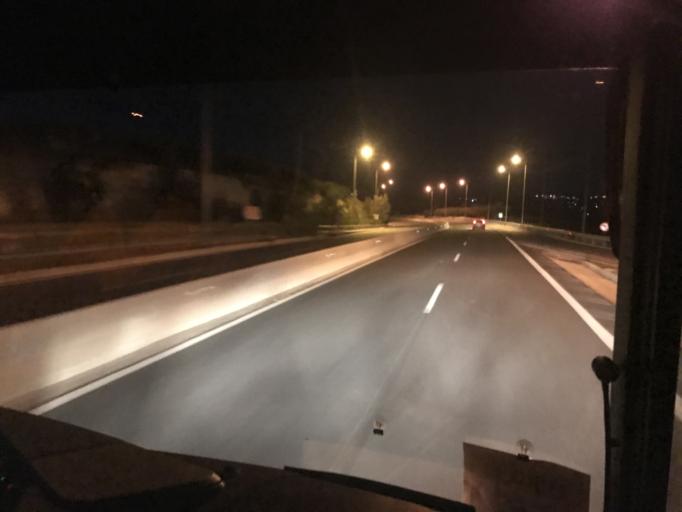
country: GR
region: Crete
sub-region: Nomos Irakleiou
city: Skalanion
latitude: 35.2645
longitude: 25.1833
